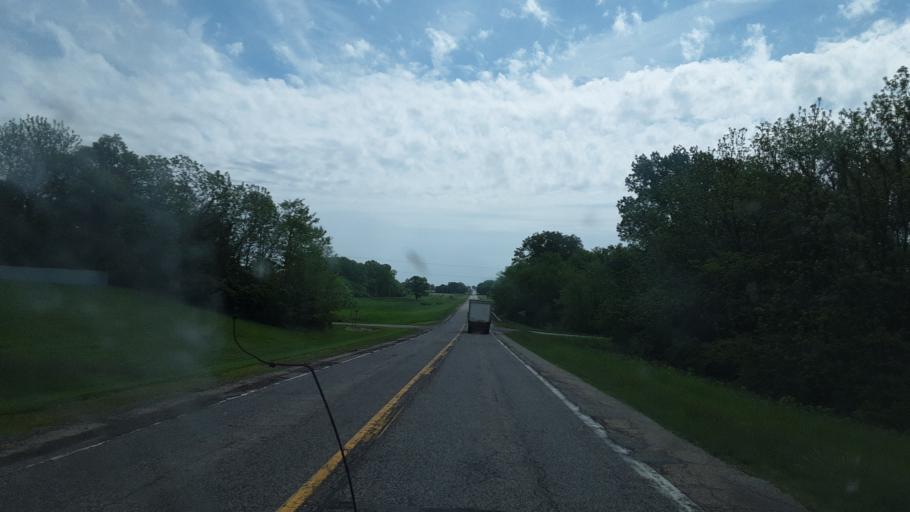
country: US
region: Illinois
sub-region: Tazewell County
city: Richmond
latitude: 40.3103
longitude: -89.3030
